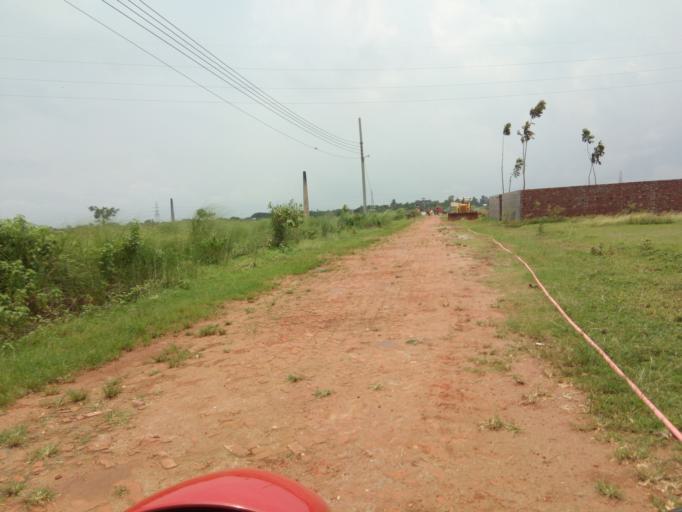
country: BD
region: Dhaka
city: Azimpur
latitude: 23.7517
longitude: 90.3339
